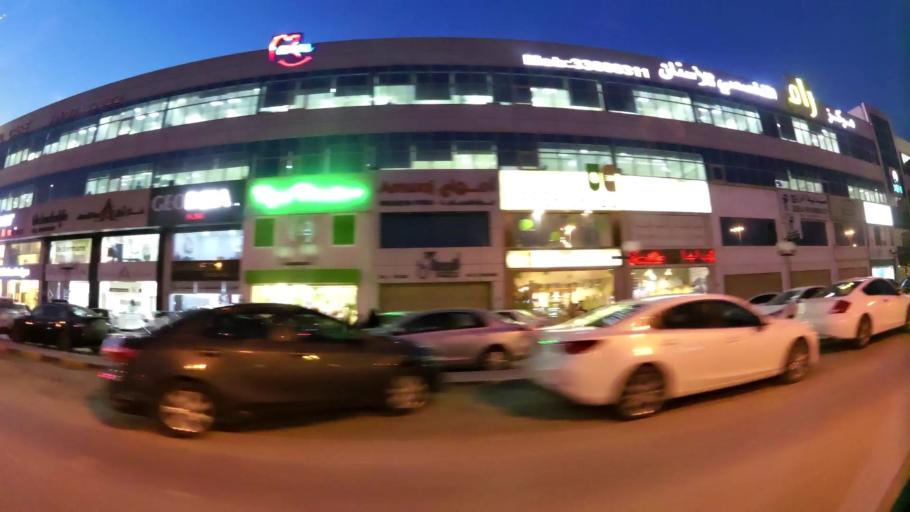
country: BH
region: Manama
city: Jidd Hafs
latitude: 26.2008
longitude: 50.5587
